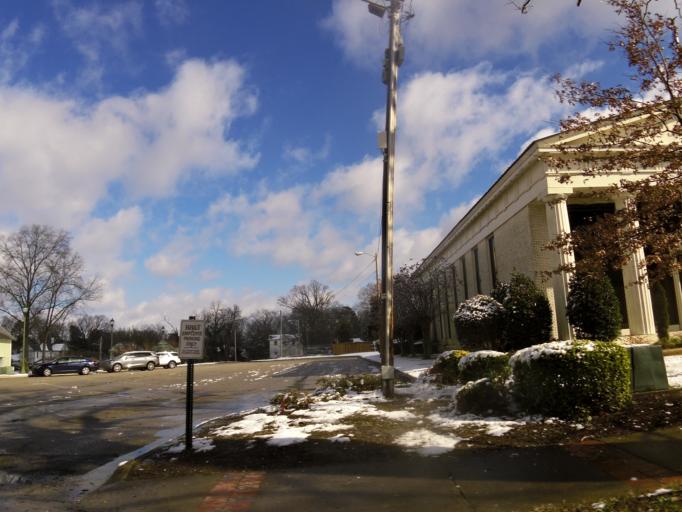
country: US
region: North Carolina
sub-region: Wilson County
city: Wilson
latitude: 35.7271
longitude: -77.9123
